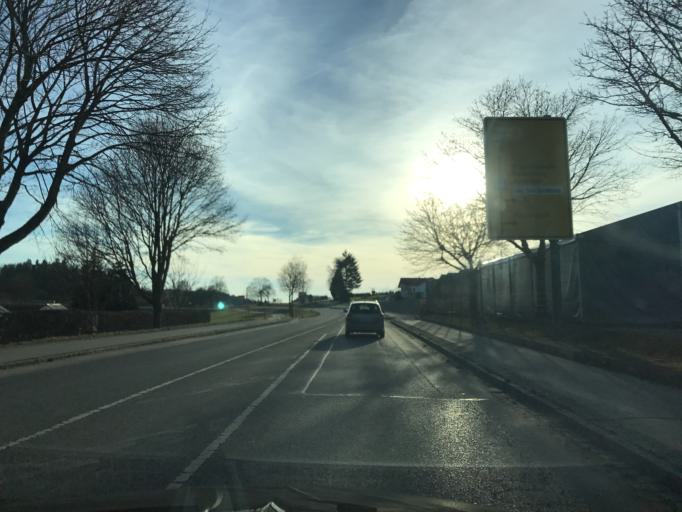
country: DE
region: Baden-Wuerttemberg
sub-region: Tuebingen Region
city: Bad Waldsee
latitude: 47.9129
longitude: 9.7445
